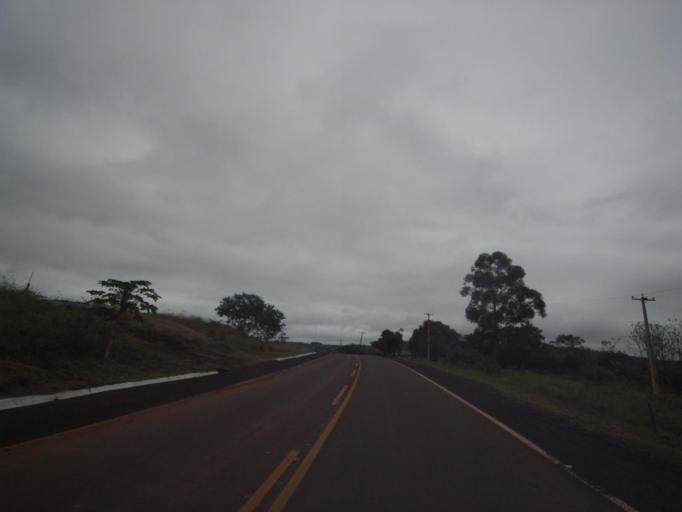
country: AR
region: Misiones
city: El Soberbio
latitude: -27.2876
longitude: -54.1877
